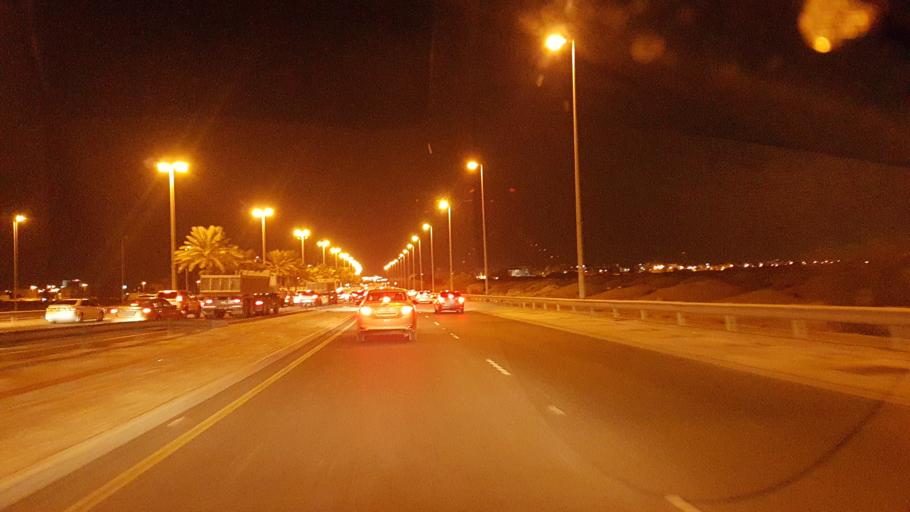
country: BH
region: Central Governorate
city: Madinat Hamad
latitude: 26.1451
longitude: 50.5102
